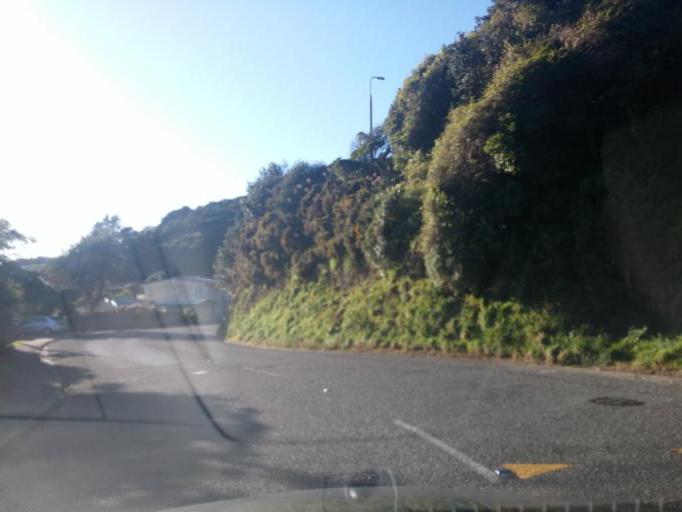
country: NZ
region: Wellington
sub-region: Wellington City
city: Kelburn
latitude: -41.2709
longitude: 174.7612
